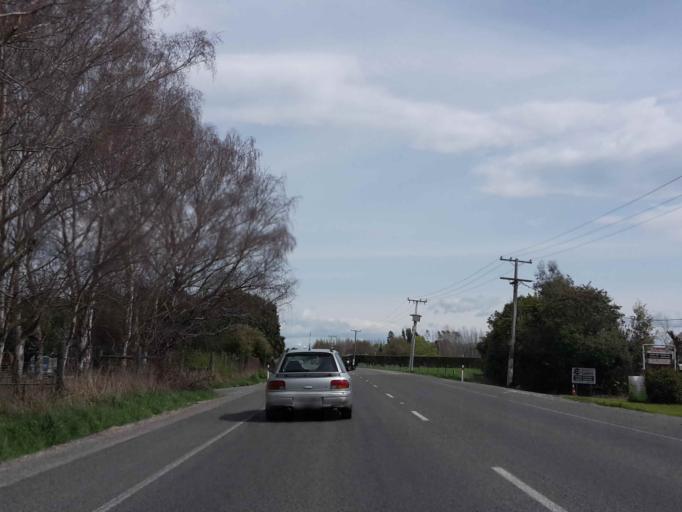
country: NZ
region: Canterbury
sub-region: Waimakariri District
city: Kaiapoi
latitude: -43.4079
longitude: 172.6373
